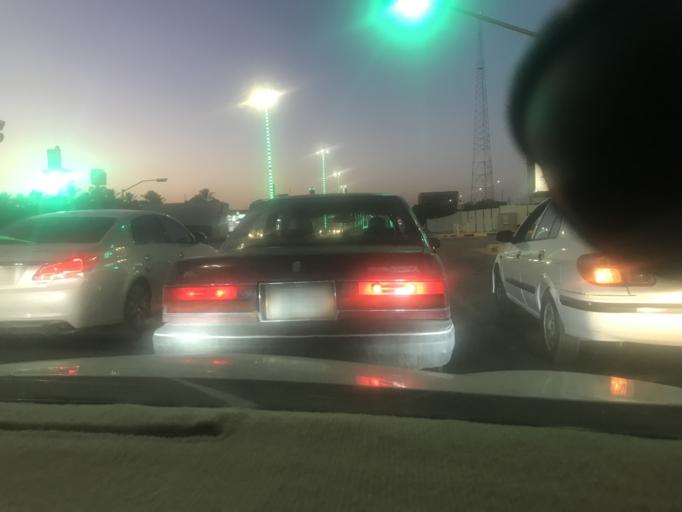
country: SA
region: Al-Qassim
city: Unaizah
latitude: 26.0818
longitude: 43.9907
